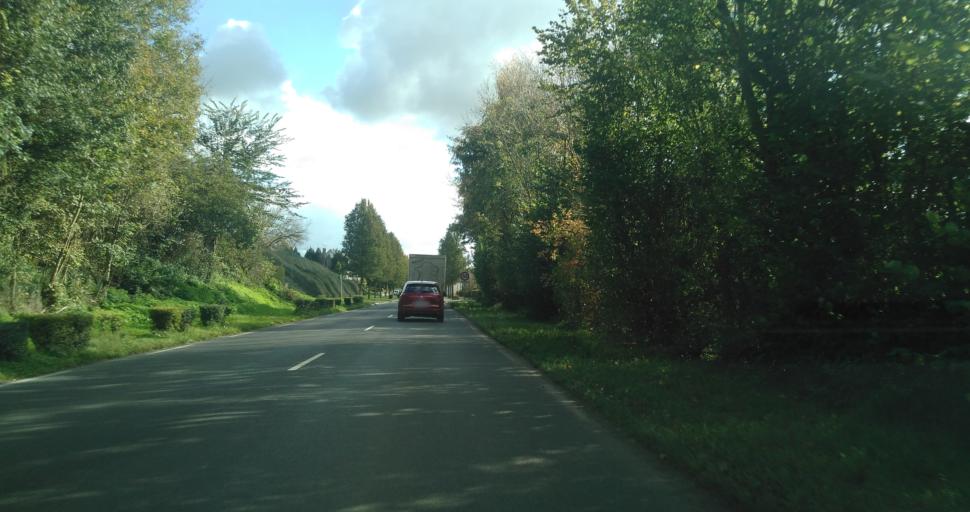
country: FR
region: Picardie
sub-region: Departement de la Somme
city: Doullens
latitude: 50.1629
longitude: 2.3274
